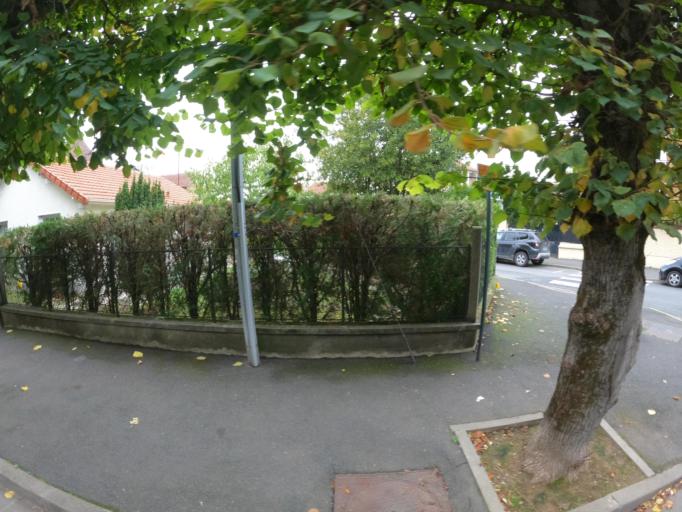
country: FR
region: Ile-de-France
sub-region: Departement de Seine-Saint-Denis
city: Gournay-sur-Marne
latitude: 48.8728
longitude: 2.5833
